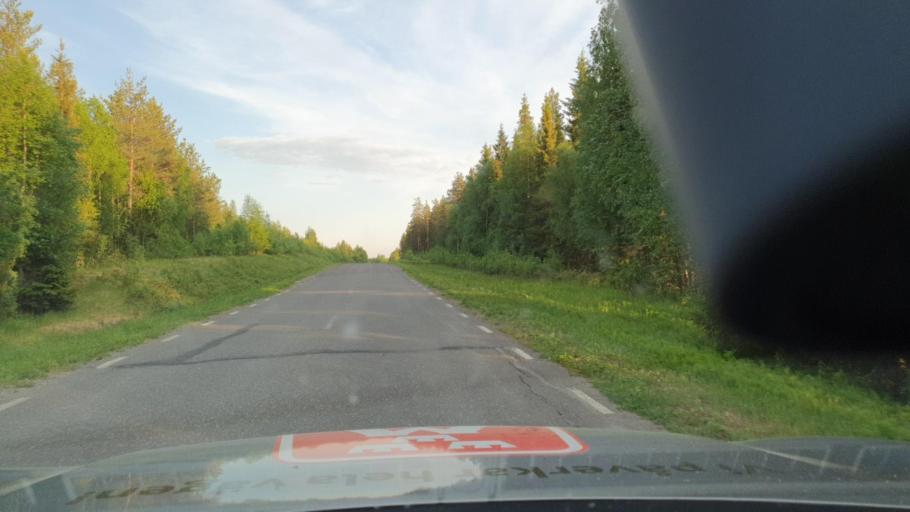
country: SE
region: Norrbotten
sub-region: Bodens Kommun
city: Boden
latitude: 66.2849
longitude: 21.3489
